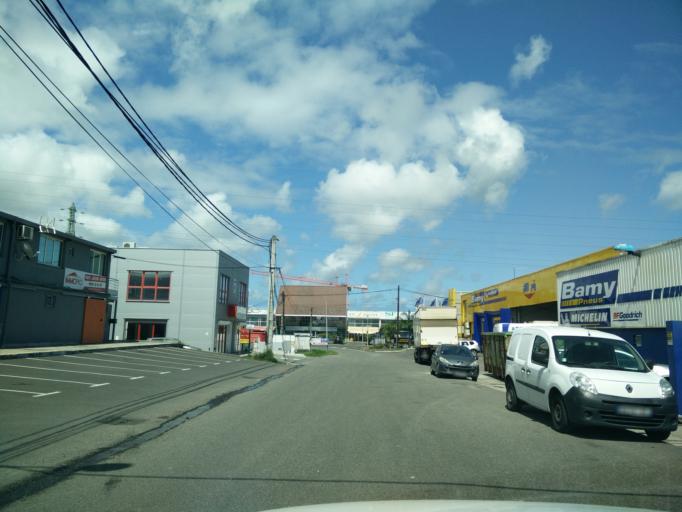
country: GP
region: Guadeloupe
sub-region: Guadeloupe
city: Pointe-a-Pitre
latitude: 16.2443
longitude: -61.5560
